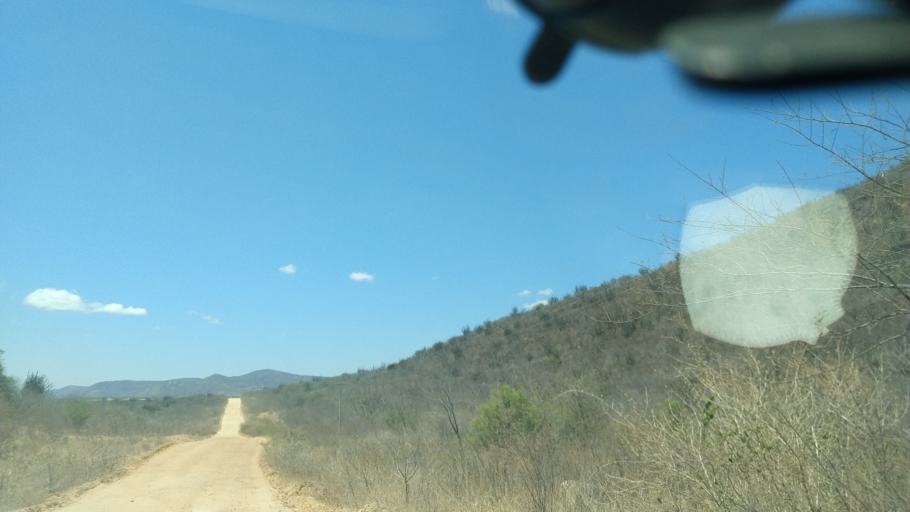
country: BR
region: Rio Grande do Norte
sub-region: Sao Tome
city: Sao Tome
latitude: -5.9695
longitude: -36.1609
